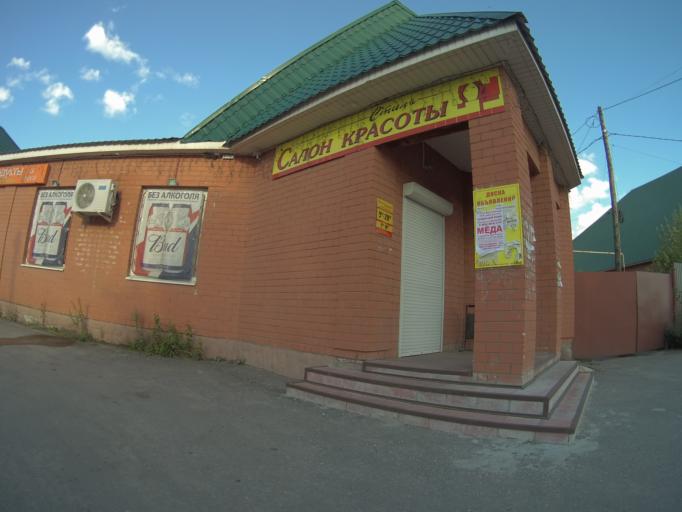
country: RU
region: Vladimir
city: Gus'-Khrustal'nyy
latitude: 55.6001
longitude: 40.6427
